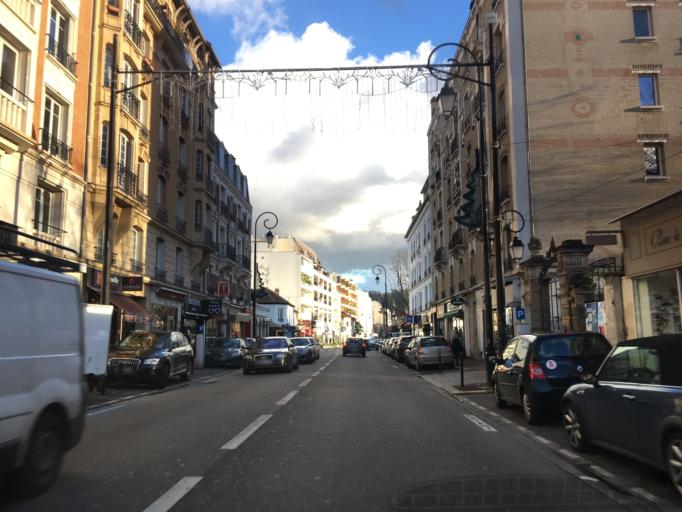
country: FR
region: Ile-de-France
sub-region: Departement du Val-de-Marne
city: Saint-Maur-des-Fosses
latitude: 48.7934
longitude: 2.5147
